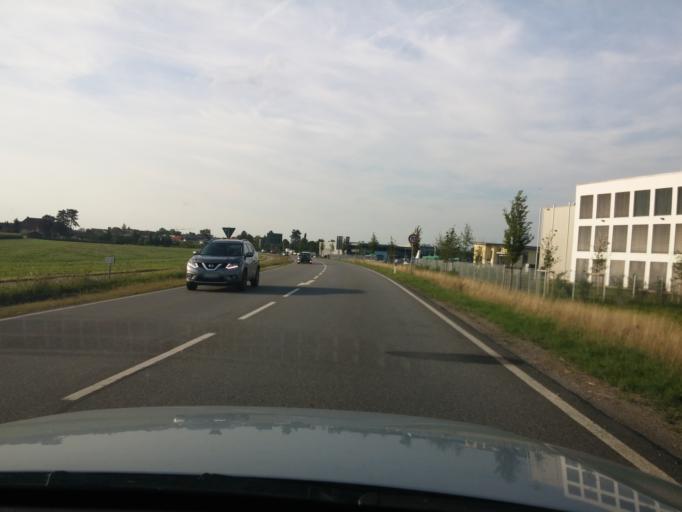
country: DE
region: Bavaria
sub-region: Upper Bavaria
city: Feldkirchen
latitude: 48.1393
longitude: 11.7361
